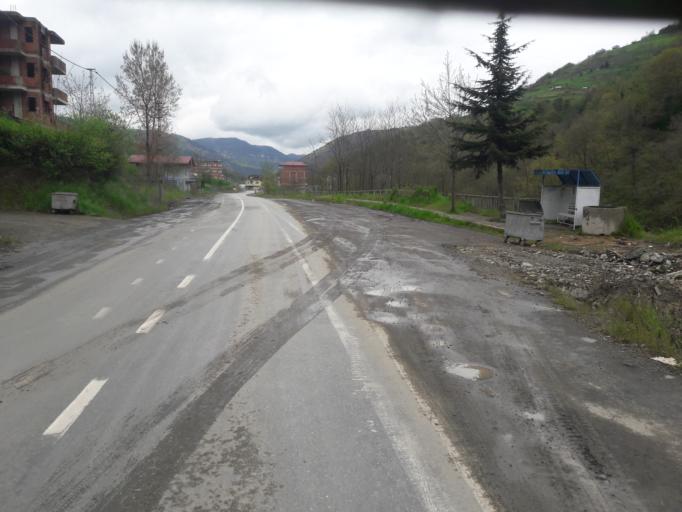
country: TR
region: Trabzon
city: Duzkoy
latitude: 40.9285
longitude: 39.4941
